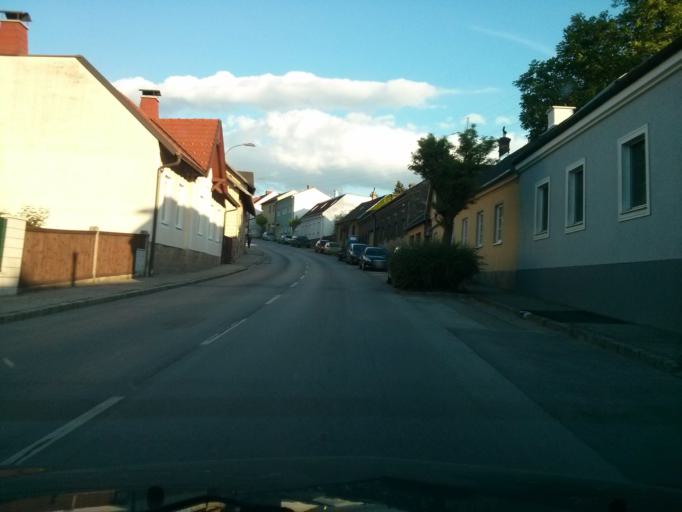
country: AT
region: Lower Austria
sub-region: Politischer Bezirk Baden
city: Hirtenberg
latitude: 47.9195
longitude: 16.1864
